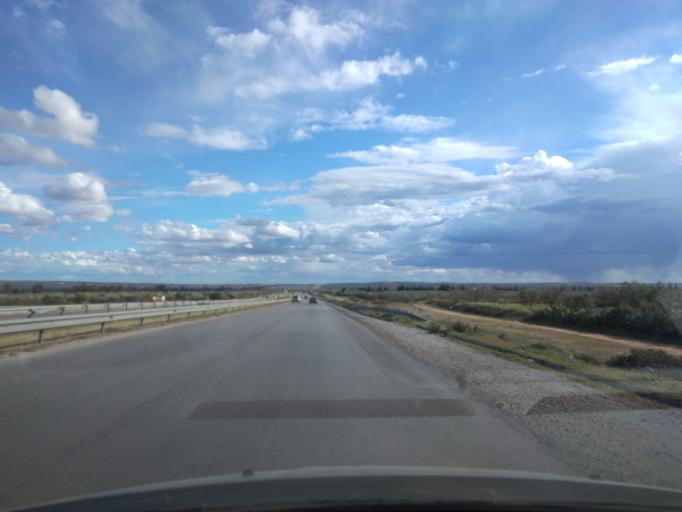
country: TN
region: Al Munastir
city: Manzil Kamil
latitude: 35.6018
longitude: 10.6001
